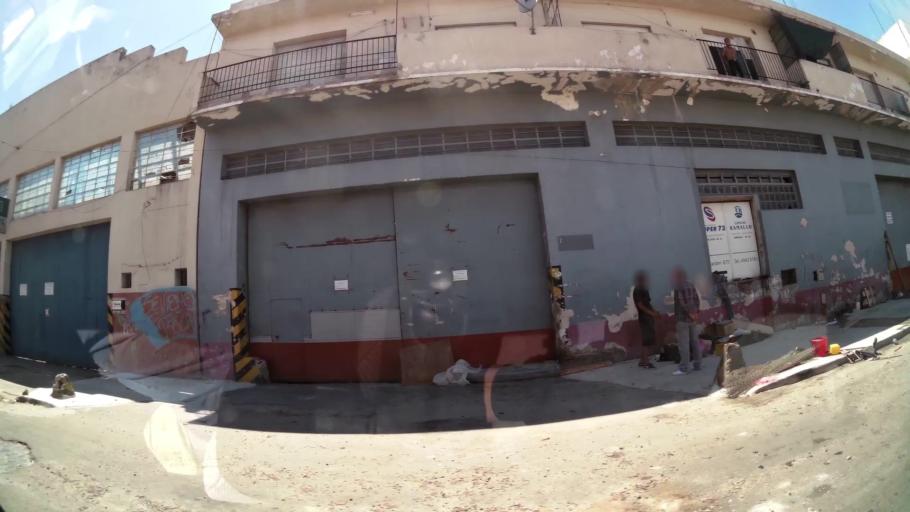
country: AR
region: Buenos Aires
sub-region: Partido de Avellaneda
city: Avellaneda
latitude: -34.6436
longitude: -58.4005
